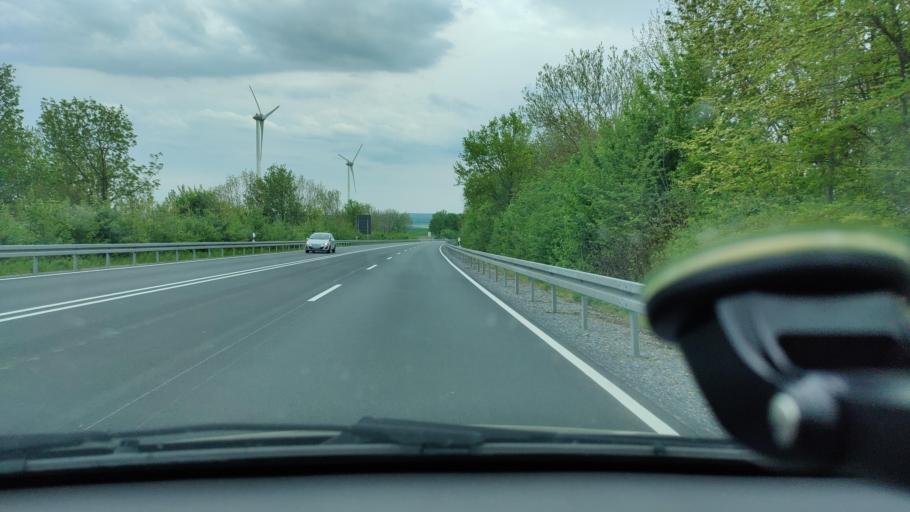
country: DE
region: North Rhine-Westphalia
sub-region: Regierungsbezirk Detmold
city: Wunnenberg
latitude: 51.5560
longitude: 8.7161
